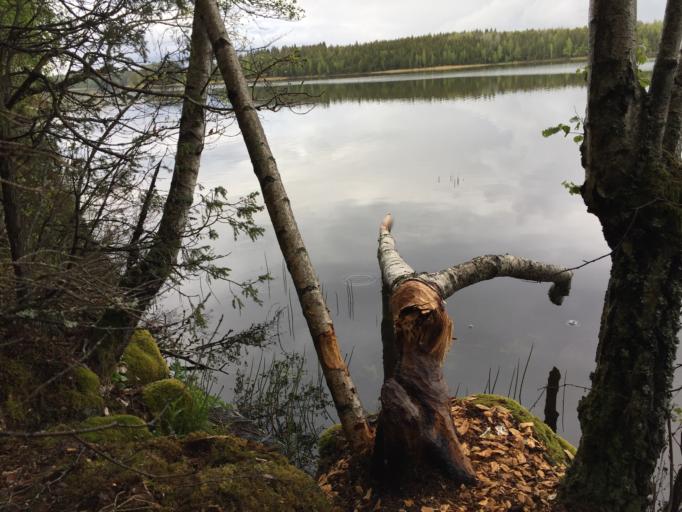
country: SE
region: OErebro
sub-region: Orebro Kommun
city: Odensbacken
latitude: 59.0002
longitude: 15.6631
